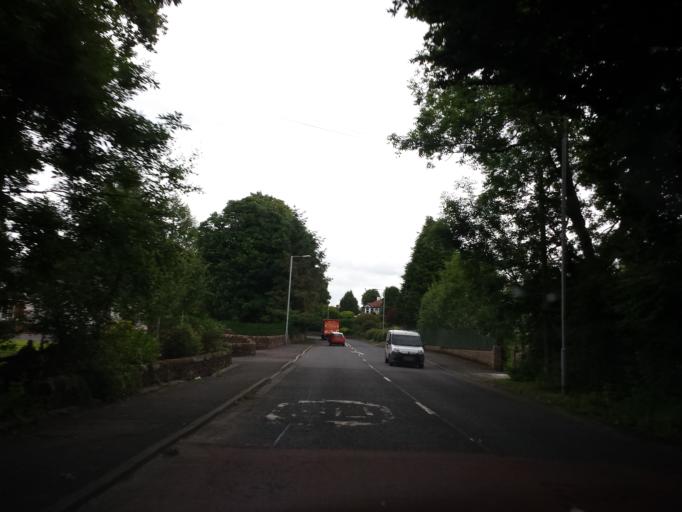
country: GB
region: Scotland
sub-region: Dumfries and Galloway
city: Dumfries
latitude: 55.0647
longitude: -3.6317
